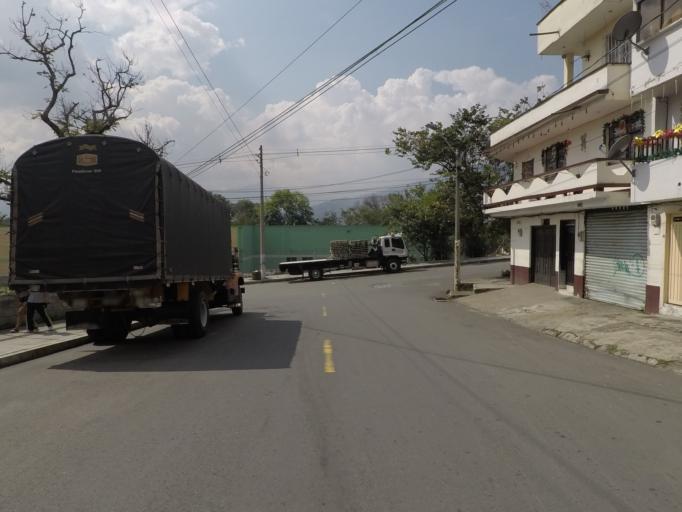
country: CO
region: Antioquia
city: Medellin
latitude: 6.2744
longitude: -75.5582
